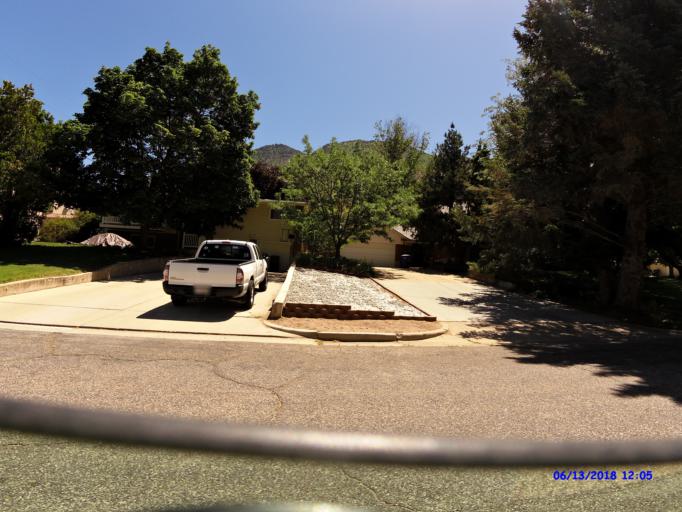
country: US
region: Utah
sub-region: Weber County
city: Ogden
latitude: 41.2279
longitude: -111.9343
